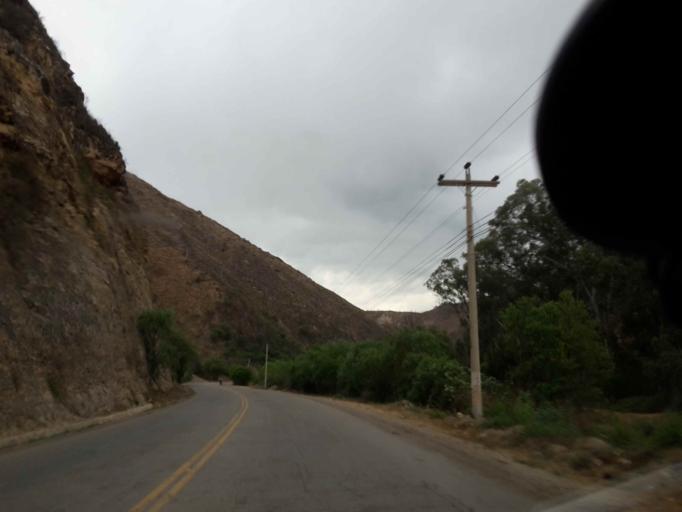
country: BO
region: Cochabamba
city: Sipe Sipe
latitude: -17.5287
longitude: -66.3357
